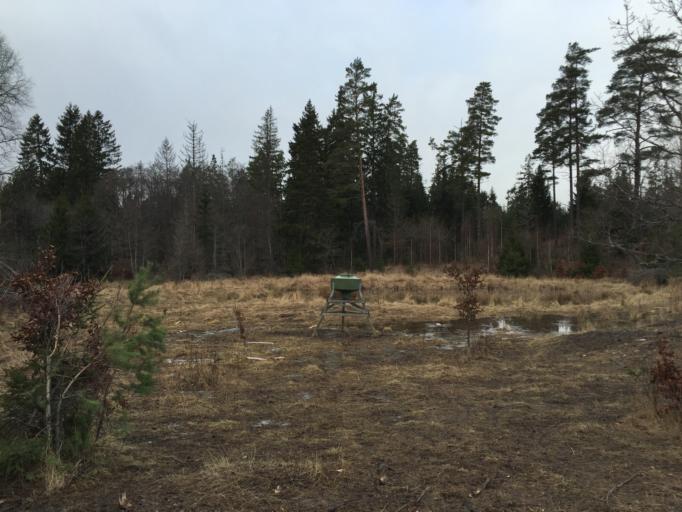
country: SE
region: Stockholm
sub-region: Salems Kommun
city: Ronninge
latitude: 59.2509
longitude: 17.7067
